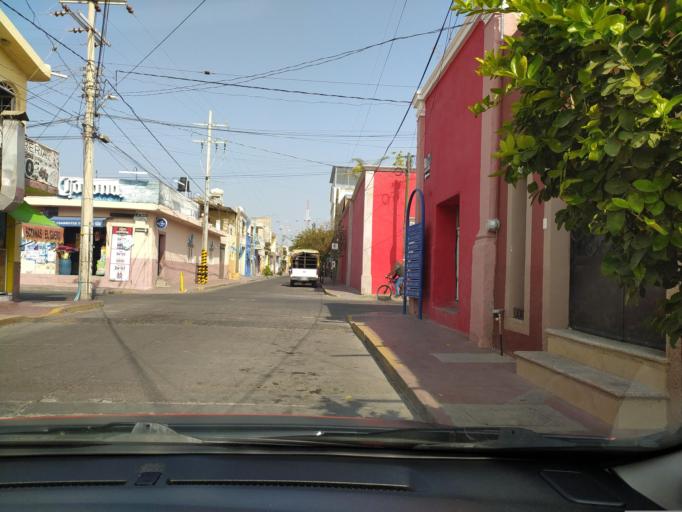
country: MX
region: Guanajuato
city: San Francisco del Rincon
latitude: 21.0286
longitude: -101.8796
